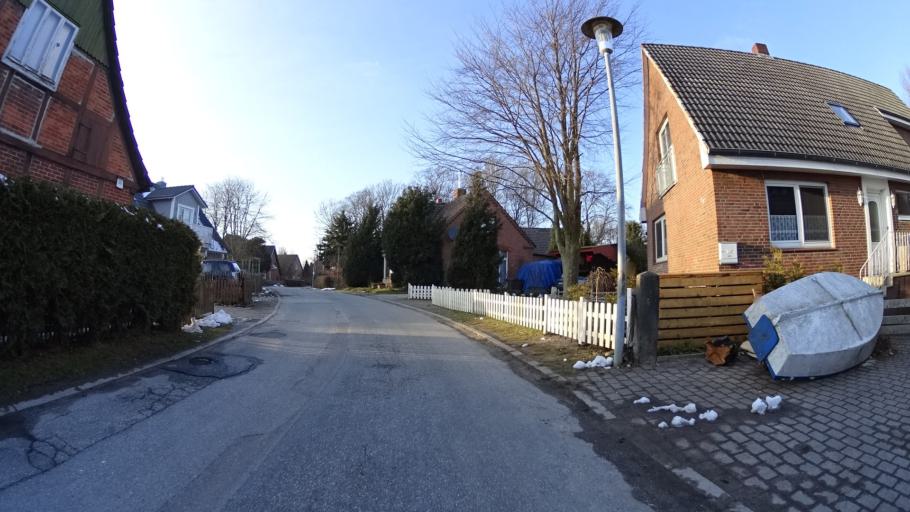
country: DE
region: Schleswig-Holstein
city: Bendfeld
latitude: 54.3656
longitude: 10.4188
